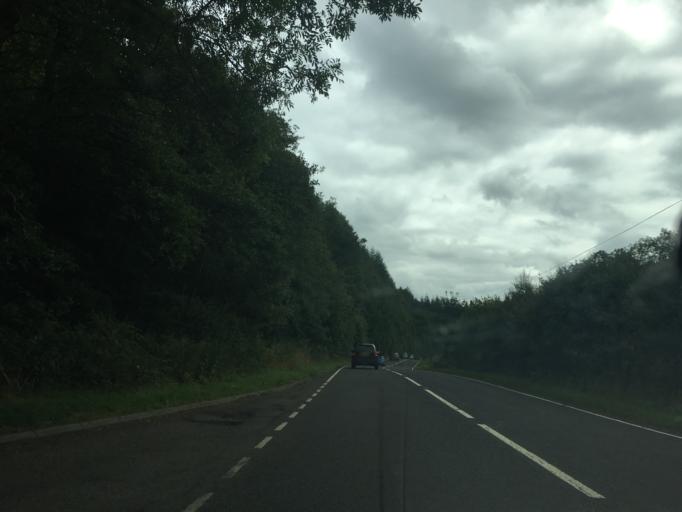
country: GB
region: Scotland
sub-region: Stirling
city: Callander
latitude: 56.3005
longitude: -4.3091
